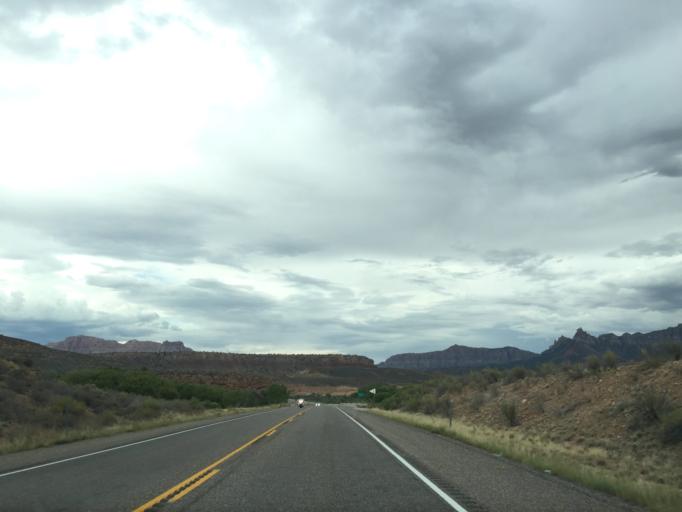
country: US
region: Utah
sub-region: Washington County
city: LaVerkin
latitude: 37.1711
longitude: -113.0851
